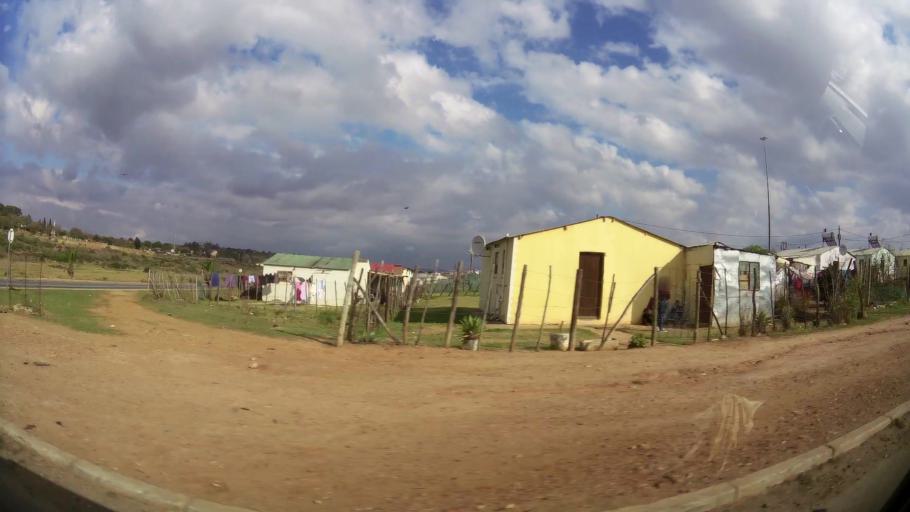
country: ZA
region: Eastern Cape
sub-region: Nelson Mandela Bay Metropolitan Municipality
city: Uitenhage
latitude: -33.7446
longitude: 25.3980
